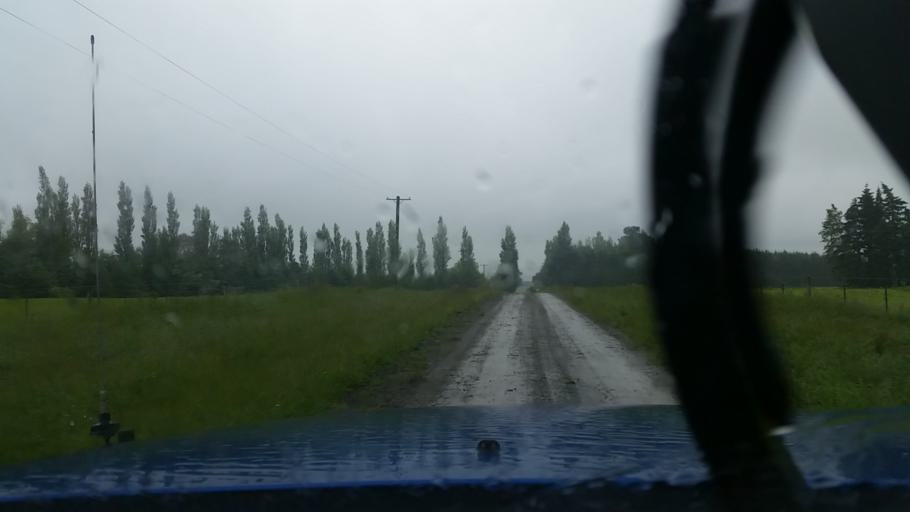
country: NZ
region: Canterbury
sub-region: Ashburton District
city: Methven
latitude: -43.7530
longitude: 171.2481
